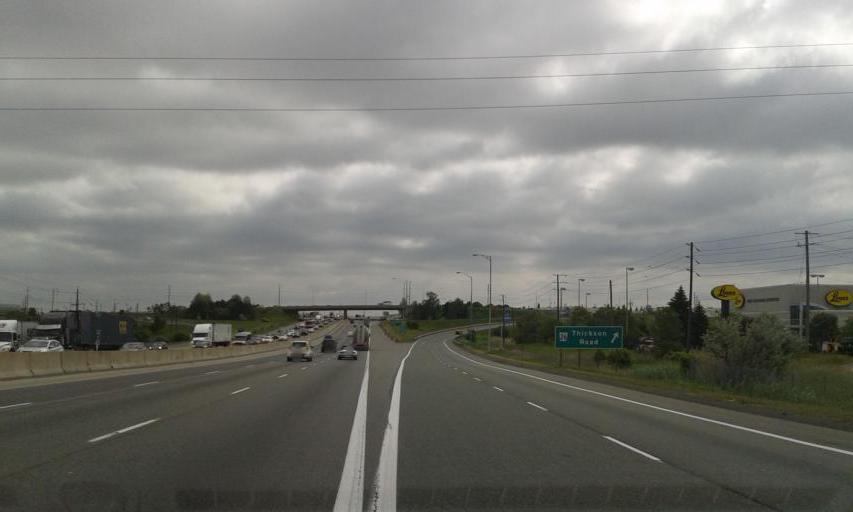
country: CA
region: Ontario
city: Oshawa
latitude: 43.8678
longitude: -78.9109
